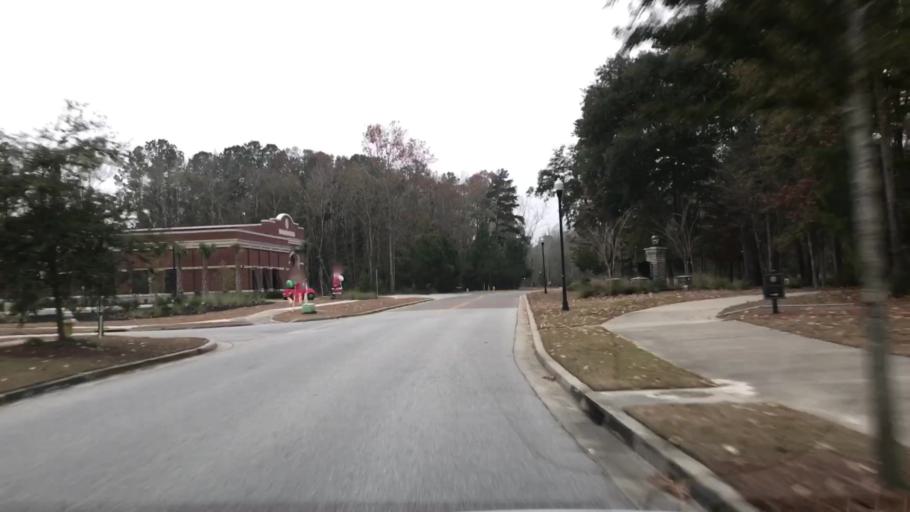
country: US
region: South Carolina
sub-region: Charleston County
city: Shell Point
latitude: 32.8082
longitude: -80.0768
